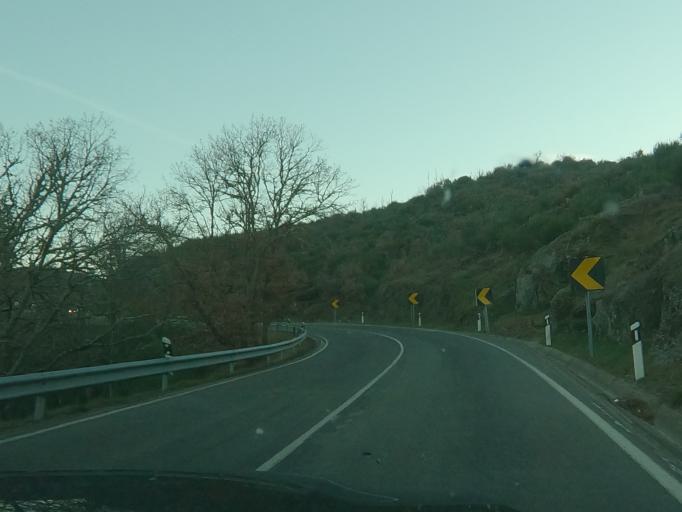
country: PT
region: Vila Real
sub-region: Vila Pouca de Aguiar
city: Vila Pouca de Aguiar
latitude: 41.4157
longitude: -7.6872
